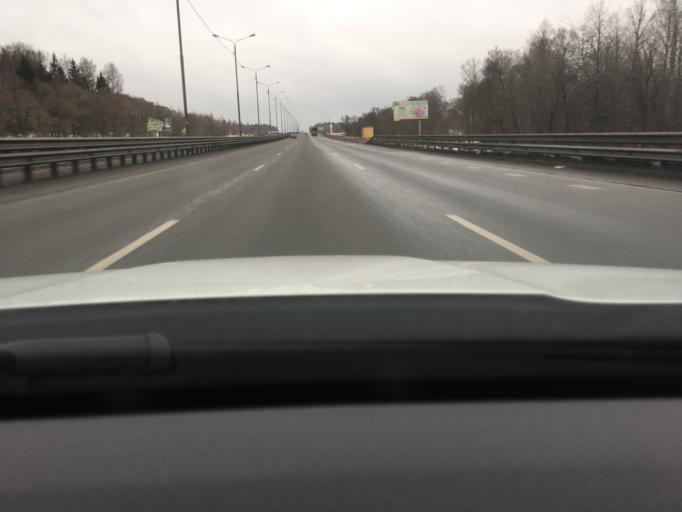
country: RU
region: Moskovskaya
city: Novyy Byt
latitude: 55.0780
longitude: 37.5757
